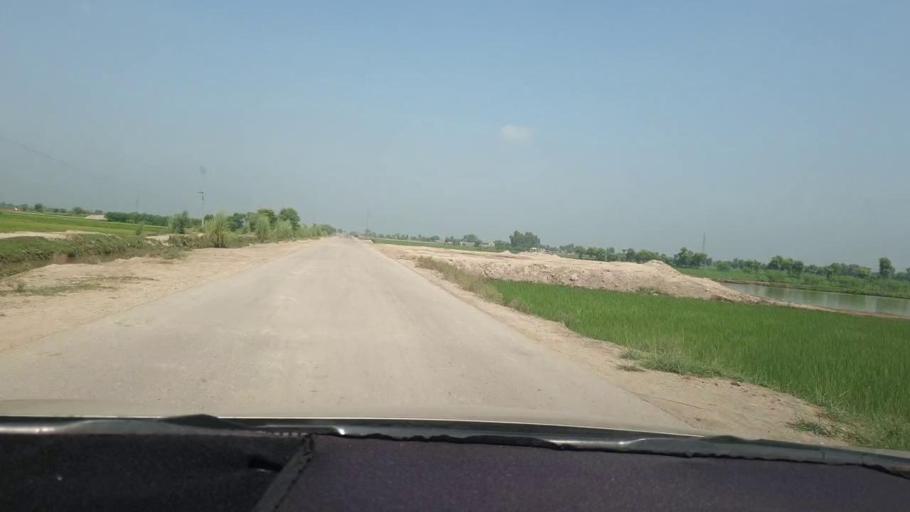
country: PK
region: Sindh
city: Miro Khan
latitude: 27.7748
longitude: 68.0577
